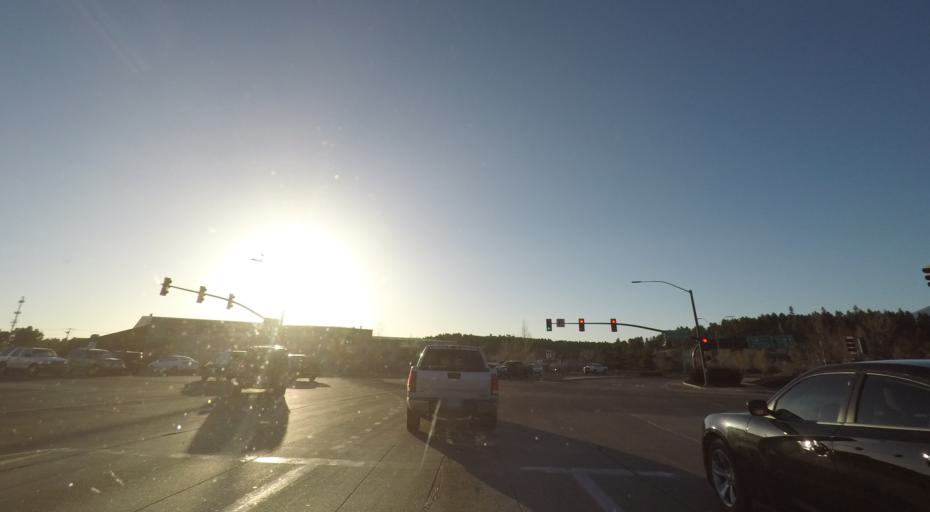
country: US
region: Arizona
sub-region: Coconino County
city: Flagstaff
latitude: 35.1921
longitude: -111.6276
